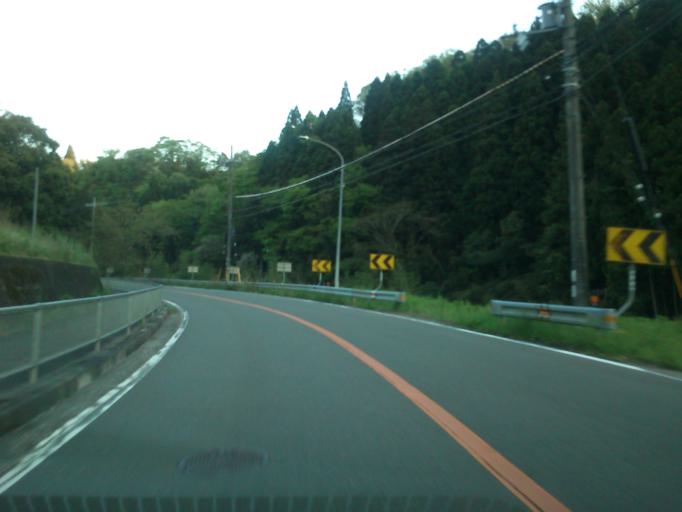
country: JP
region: Kyoto
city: Ayabe
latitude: 35.2166
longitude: 135.4199
